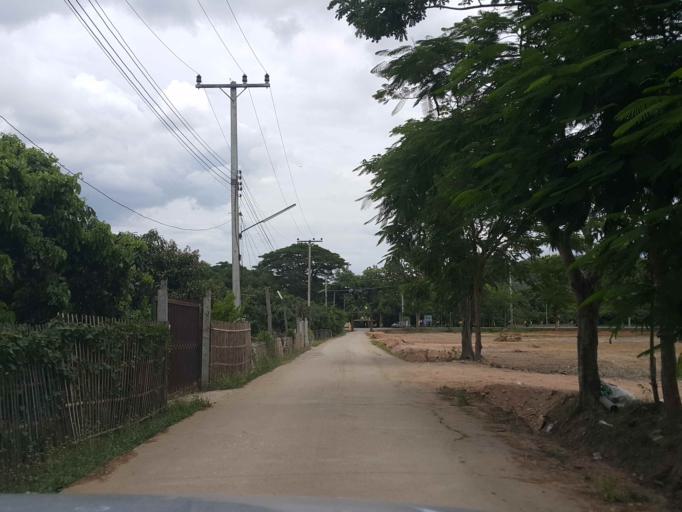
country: TH
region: Lamphun
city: Pa Sang
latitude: 18.4619
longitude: 98.9146
